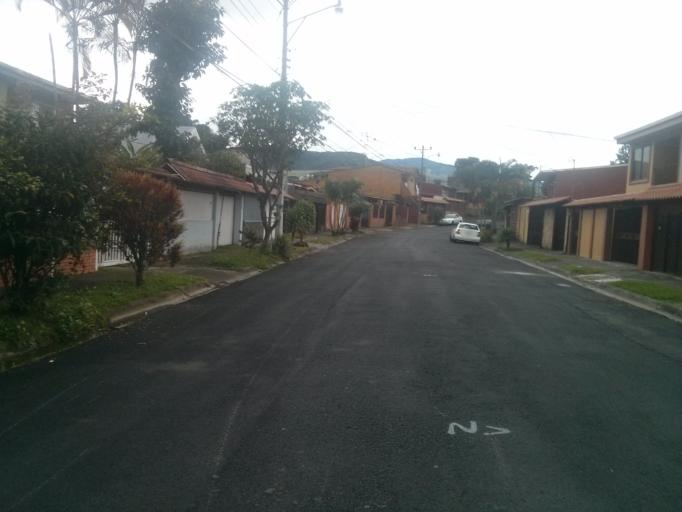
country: CR
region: San Jose
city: Curridabat
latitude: 9.9017
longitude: -84.0552
